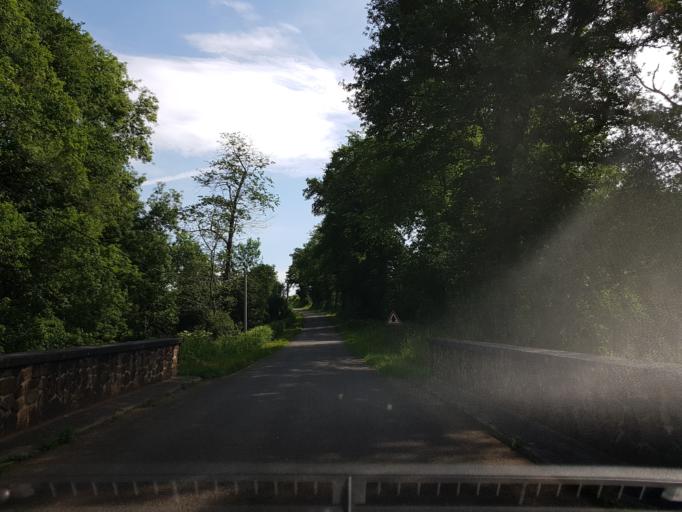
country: FR
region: Poitou-Charentes
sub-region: Departement de la Charente
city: Chabanais
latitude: 45.9291
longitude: 0.7260
